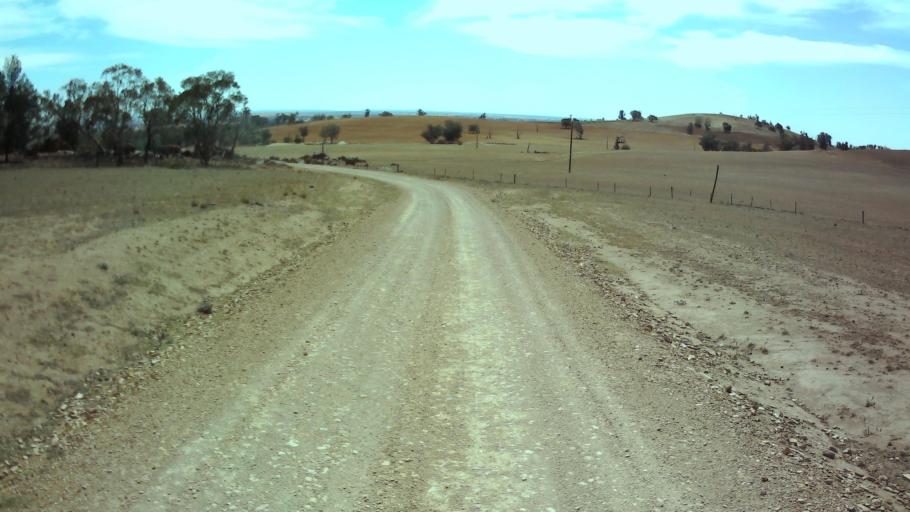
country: AU
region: New South Wales
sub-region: Weddin
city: Grenfell
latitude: -33.7423
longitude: 148.1793
